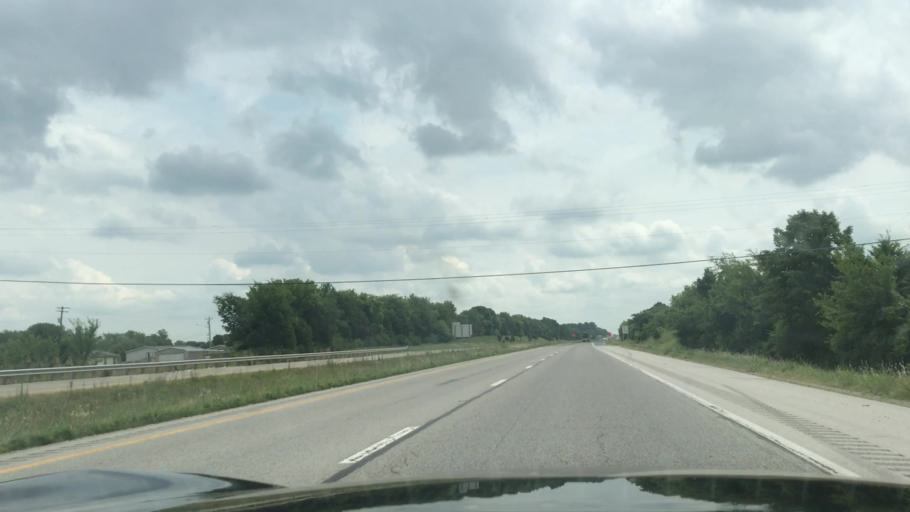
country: US
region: Kentucky
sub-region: Warren County
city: Bowling Green
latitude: 36.9887
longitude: -86.5033
